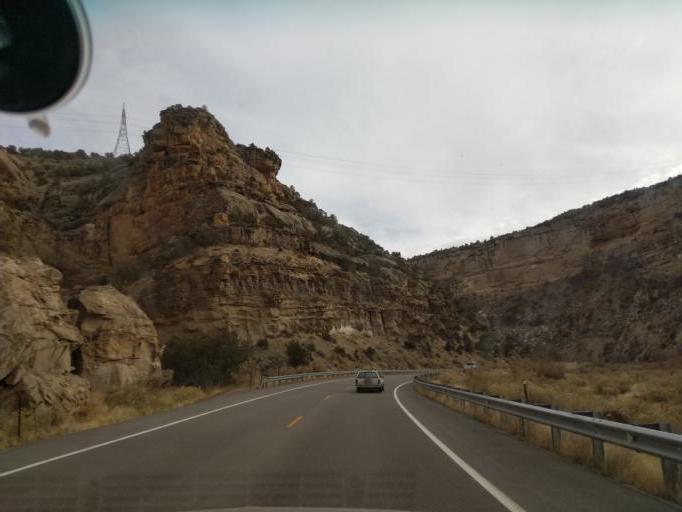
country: US
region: Colorado
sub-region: Mesa County
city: Palisade
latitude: 39.1940
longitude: -108.2372
